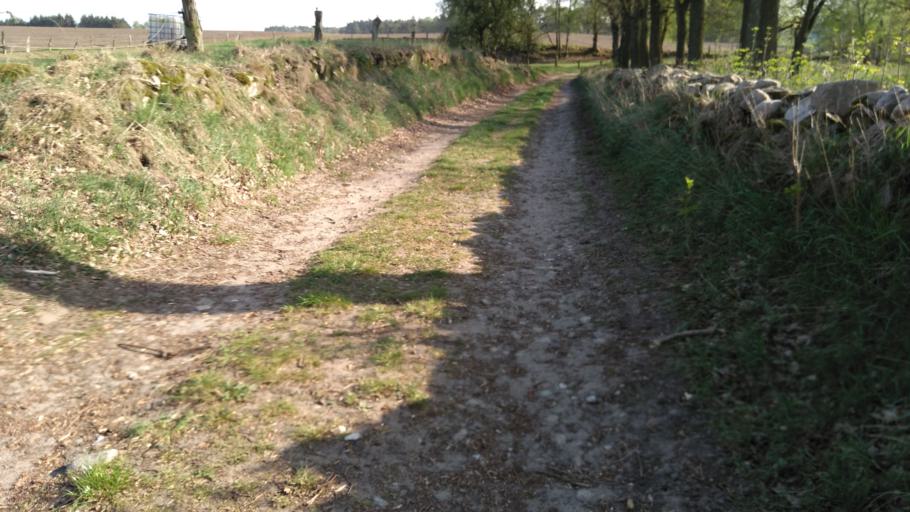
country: DE
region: Lower Saxony
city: Buxtehude
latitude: 53.4359
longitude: 9.6752
